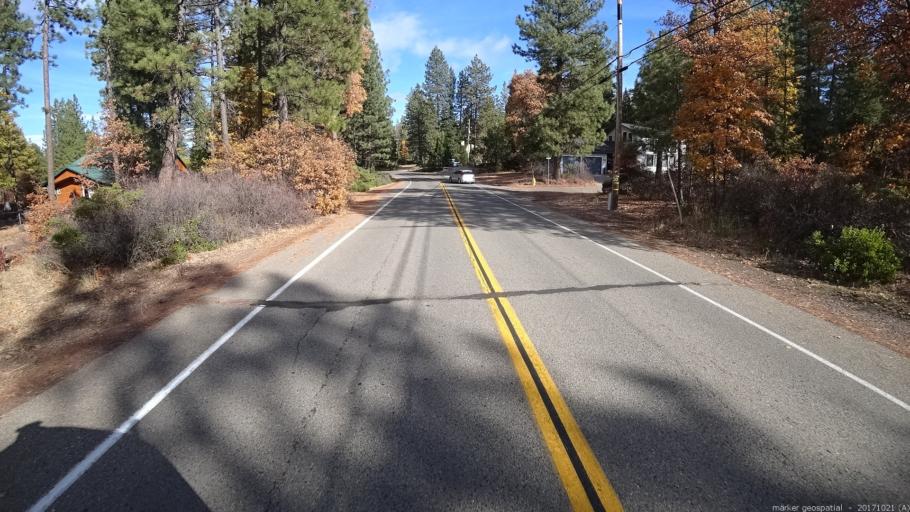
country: US
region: California
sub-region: Shasta County
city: Burney
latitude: 40.8762
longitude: -121.6637
